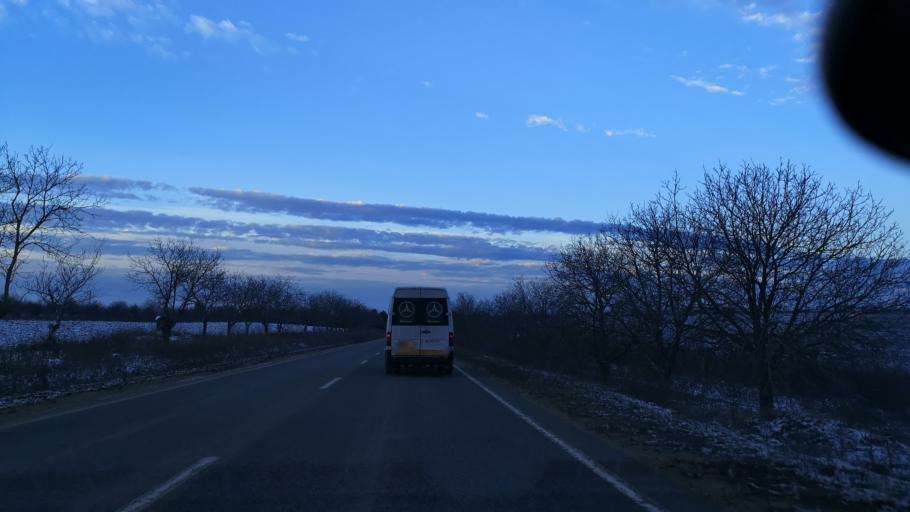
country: MD
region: Orhei
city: Orhei
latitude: 47.5445
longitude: 28.7928
